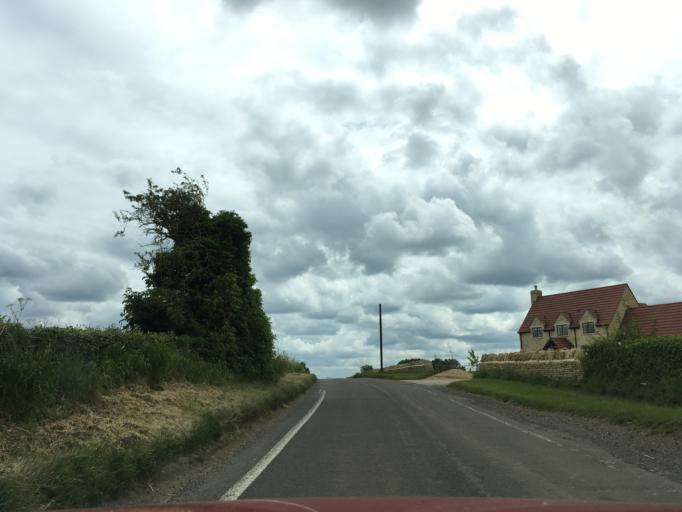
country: GB
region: England
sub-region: South Gloucestershire
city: Horton
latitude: 51.5230
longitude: -2.3360
